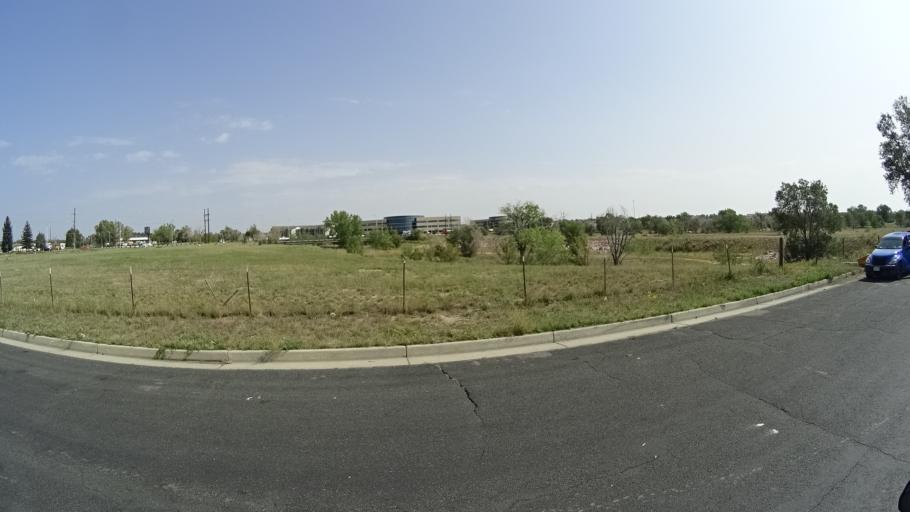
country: US
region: Colorado
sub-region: El Paso County
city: Cimarron Hills
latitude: 38.8378
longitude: -104.7300
